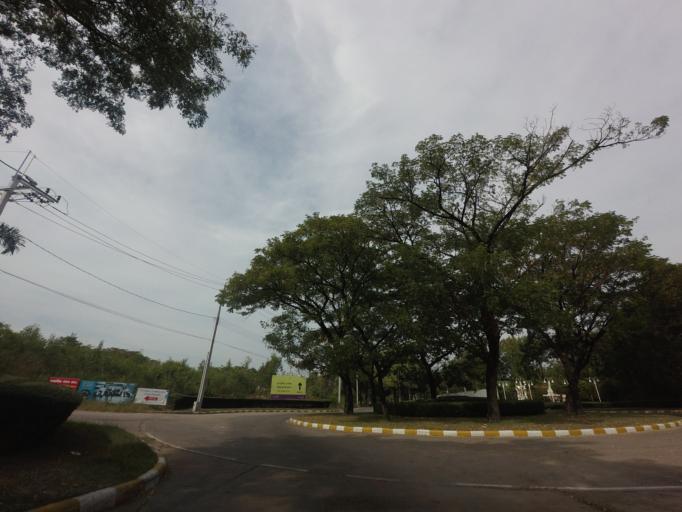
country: TH
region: Bangkok
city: Khlong Sam Wa
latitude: 13.8690
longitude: 100.7067
